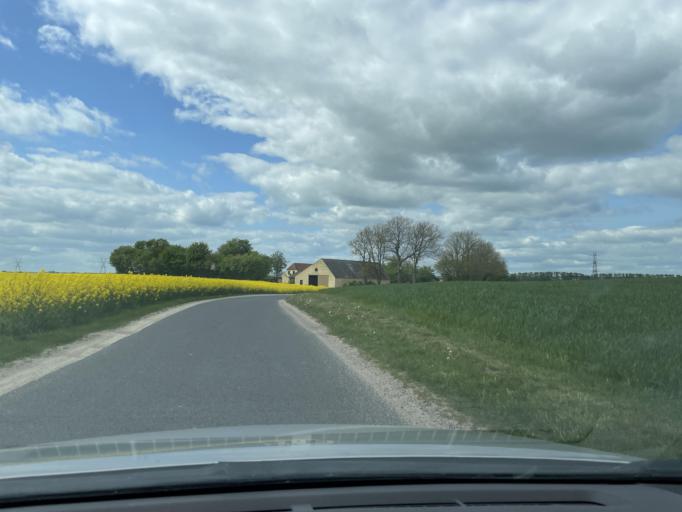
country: DK
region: Central Jutland
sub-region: Skanderborg Kommune
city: Skanderborg
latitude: 55.9217
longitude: 9.9624
